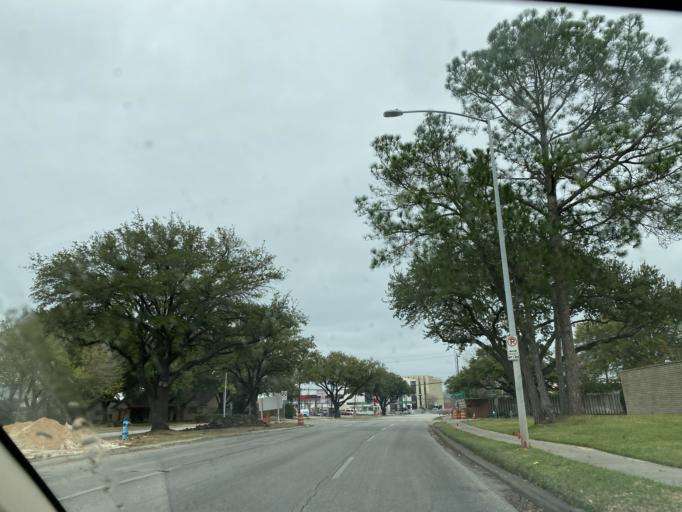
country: US
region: Texas
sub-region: Harris County
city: Piney Point Village
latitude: 29.7312
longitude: -95.5033
